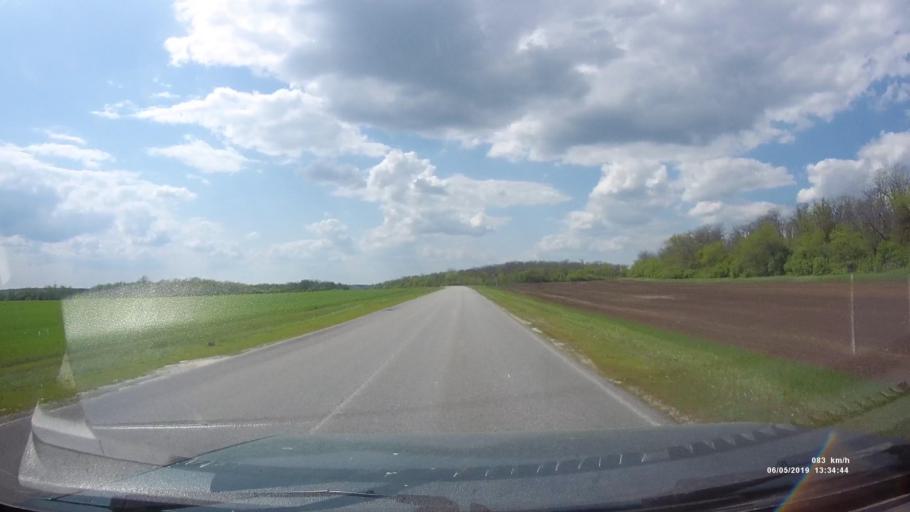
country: RU
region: Rostov
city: Ust'-Donetskiy
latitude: 47.6935
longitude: 40.7577
